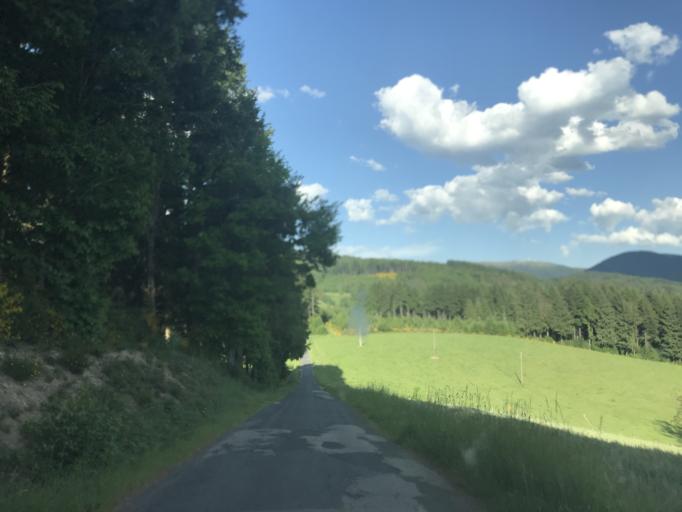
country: FR
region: Auvergne
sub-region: Departement du Puy-de-Dome
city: Job
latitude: 45.6778
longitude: 3.6891
